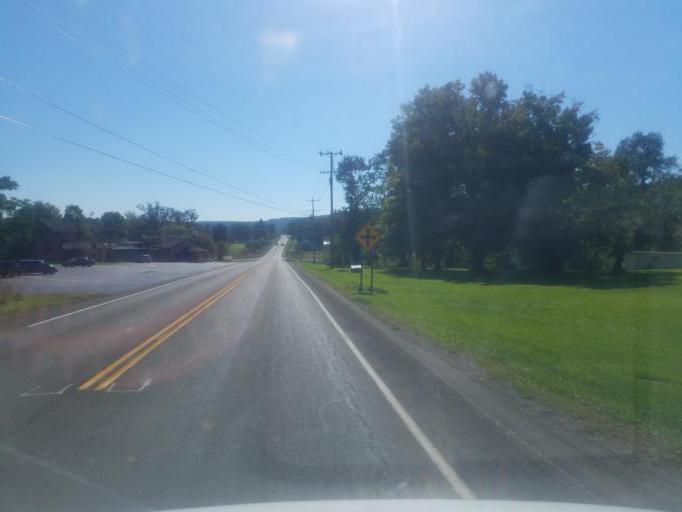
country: US
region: New York
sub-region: Allegany County
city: Cuba
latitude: 42.2433
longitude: -78.2725
